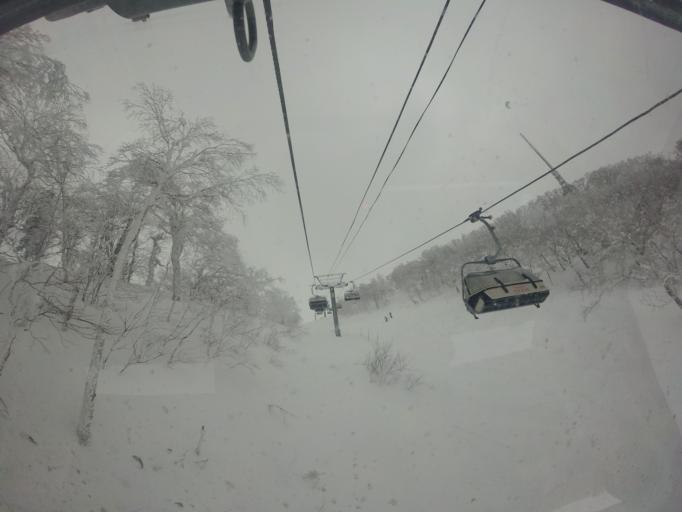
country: JP
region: Hokkaido
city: Sapporo
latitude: 43.0766
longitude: 141.1979
